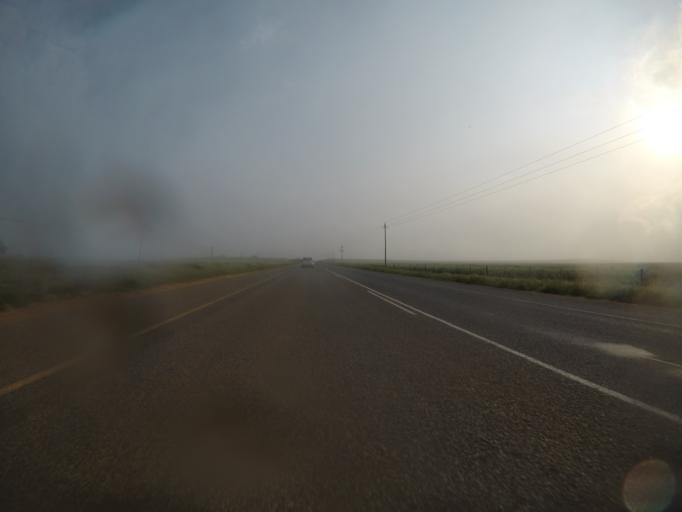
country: ZA
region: Western Cape
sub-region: City of Cape Town
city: Kraaifontein
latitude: -33.6655
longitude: 18.7076
